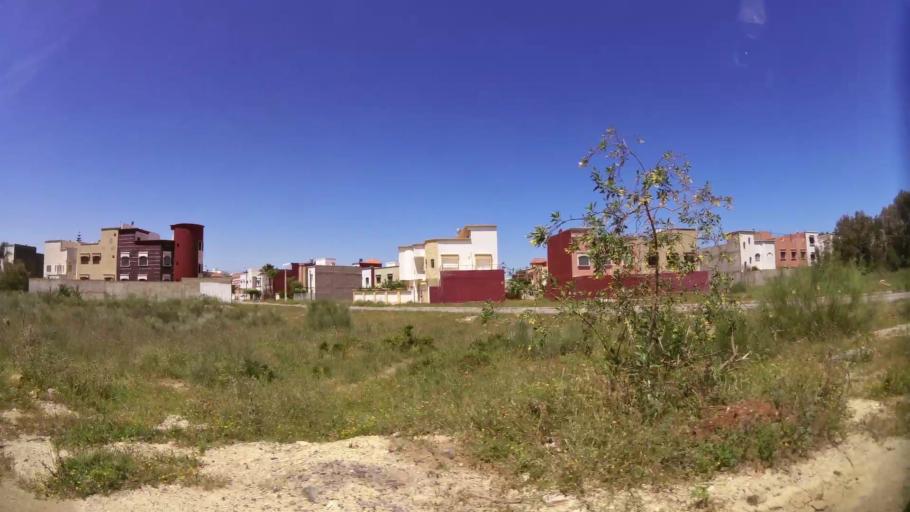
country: MA
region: Oriental
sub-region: Berkane-Taourirt
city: Madagh
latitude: 35.0873
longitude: -2.2445
